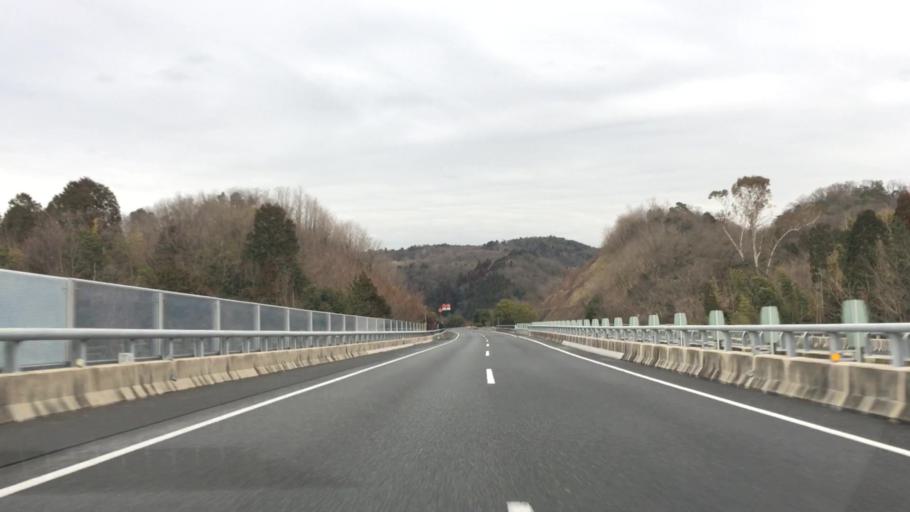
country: JP
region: Aichi
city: Seto
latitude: 35.2565
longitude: 137.1477
